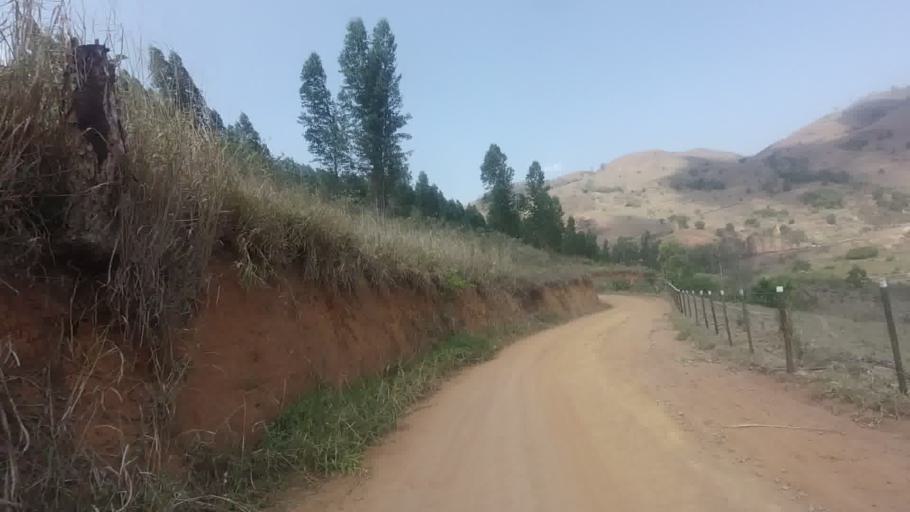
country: BR
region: Espirito Santo
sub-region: Sao Jose Do Calcado
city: Sao Jose do Calcado
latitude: -21.0435
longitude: -41.5262
